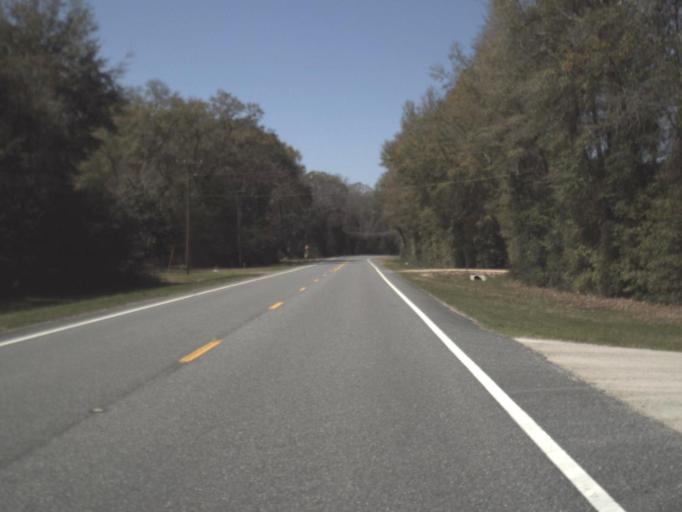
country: US
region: Florida
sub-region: Leon County
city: Woodville
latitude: 30.2382
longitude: -84.2633
